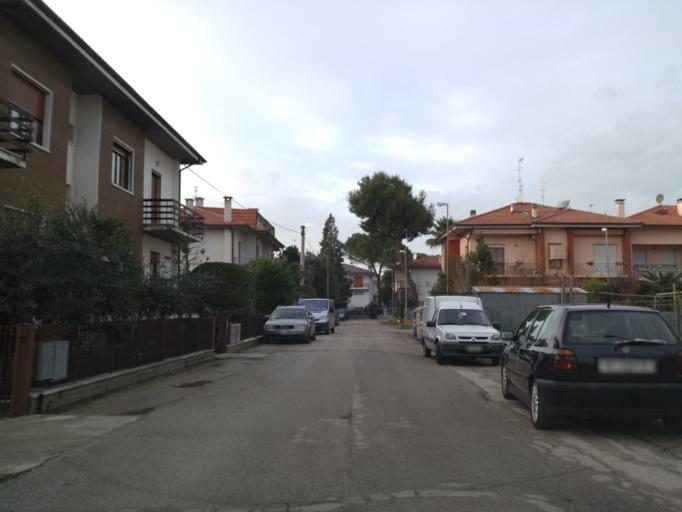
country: IT
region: The Marches
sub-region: Provincia di Pesaro e Urbino
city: Centinarola
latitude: 43.8300
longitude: 13.0014
